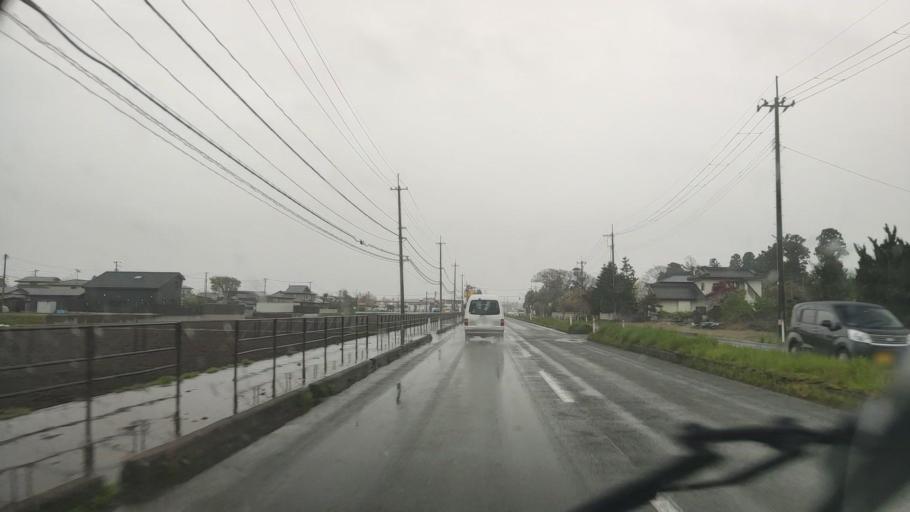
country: JP
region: Akita
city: Tenno
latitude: 39.8683
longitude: 140.0012
